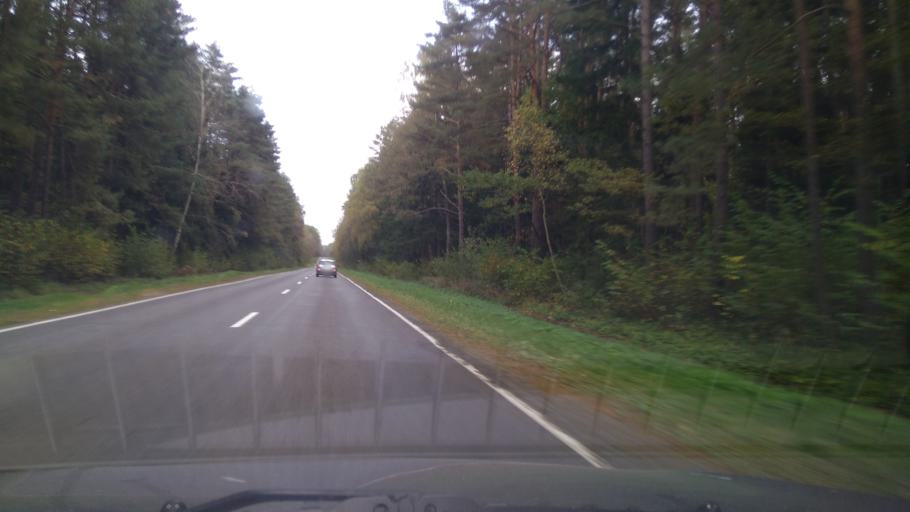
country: BY
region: Minsk
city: Druzhny
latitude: 53.6294
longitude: 27.8802
